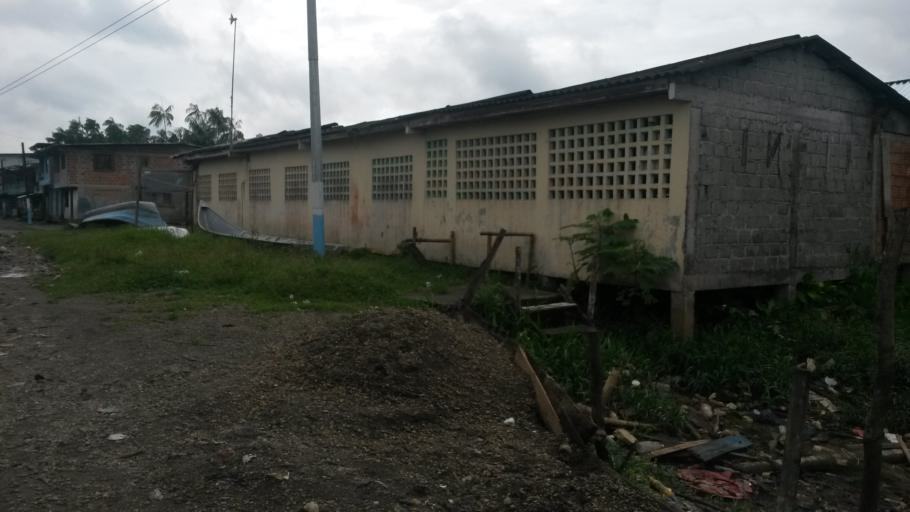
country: CO
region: Cauca
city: Guapi
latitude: 2.5673
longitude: -77.8835
